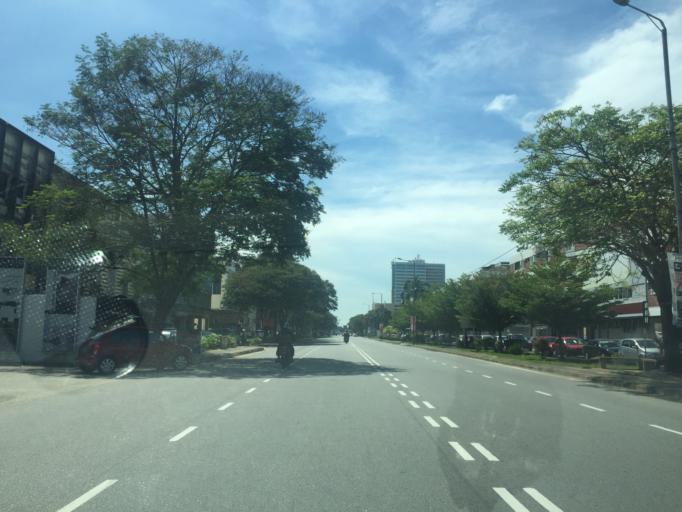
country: MY
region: Penang
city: Butterworth
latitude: 5.4020
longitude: 100.3686
